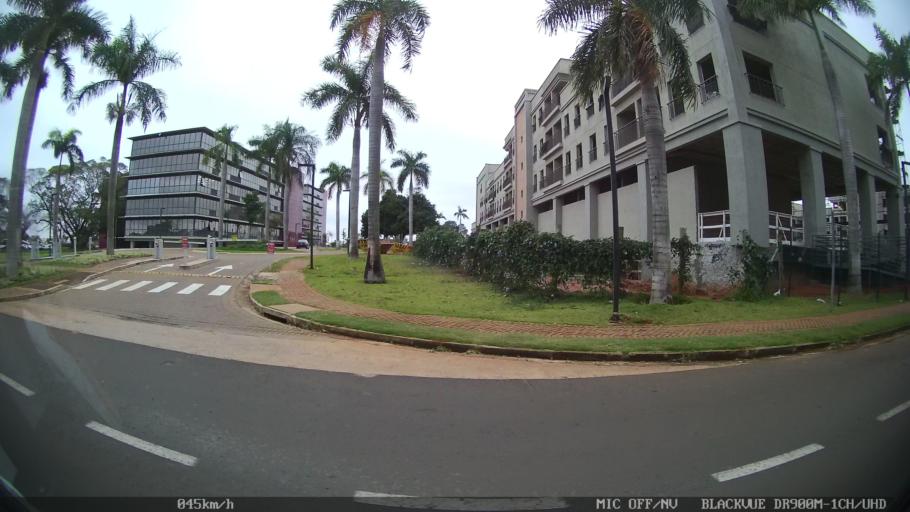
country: BR
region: Sao Paulo
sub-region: Sao Jose Do Rio Preto
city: Sao Jose do Rio Preto
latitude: -20.8468
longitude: -49.4028
